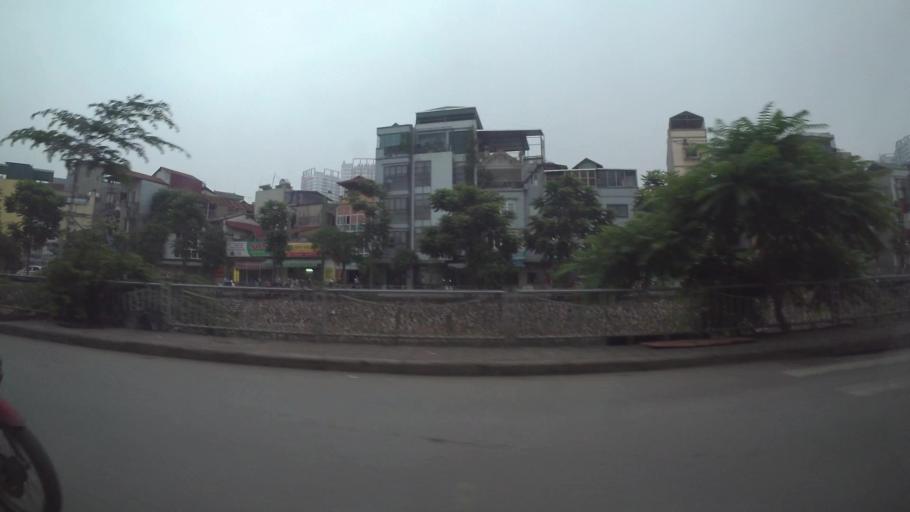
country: VN
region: Ha Noi
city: Hai BaTrung
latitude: 20.9881
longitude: 105.8371
